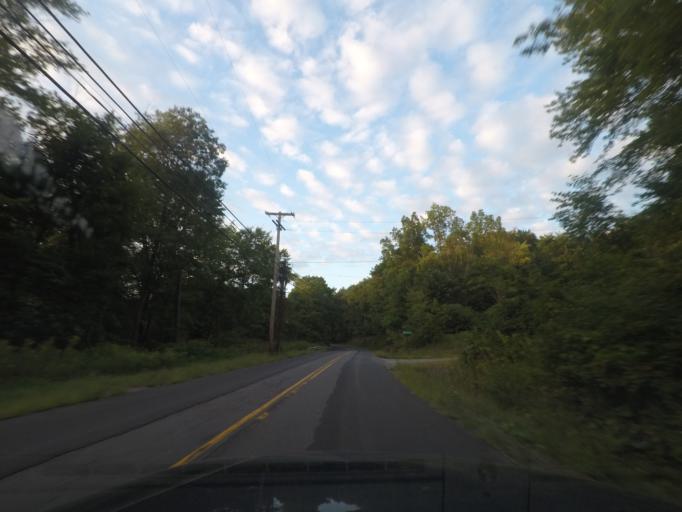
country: US
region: New York
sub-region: Rensselaer County
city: Nassau
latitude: 42.5282
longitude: -73.6021
